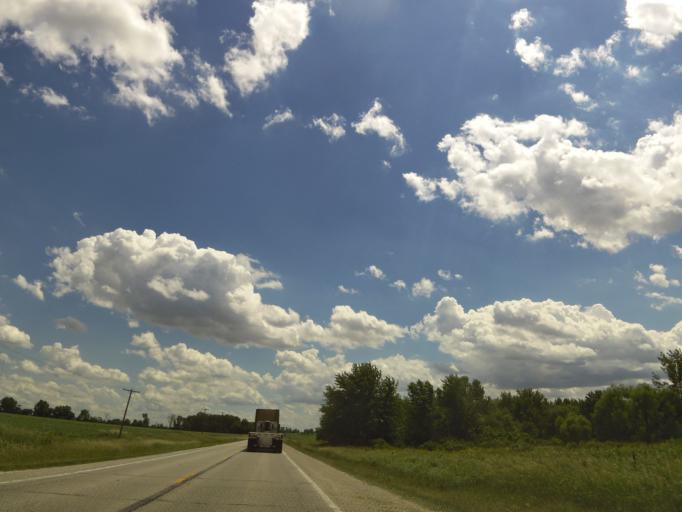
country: US
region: Iowa
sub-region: Buchanan County
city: Independence
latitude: 42.3581
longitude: -91.8894
